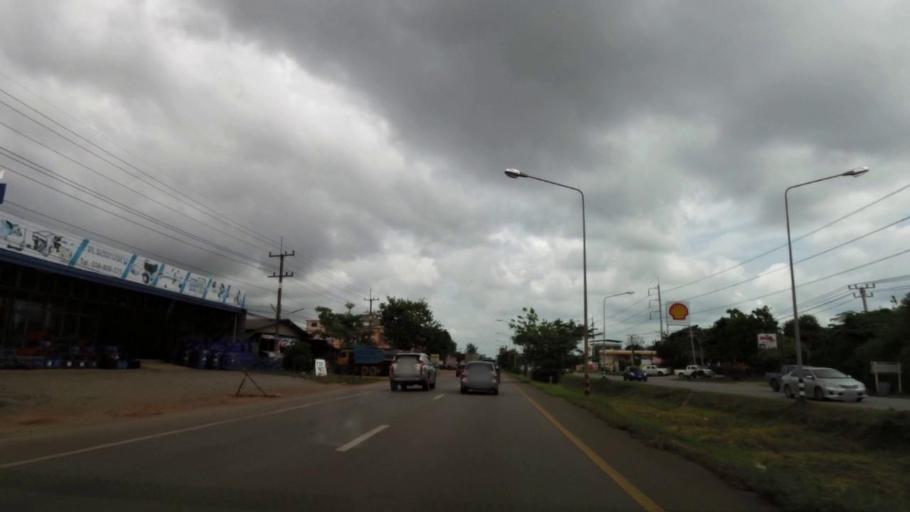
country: TH
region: Chanthaburi
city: Na Yai Am
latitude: 12.7809
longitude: 101.8160
